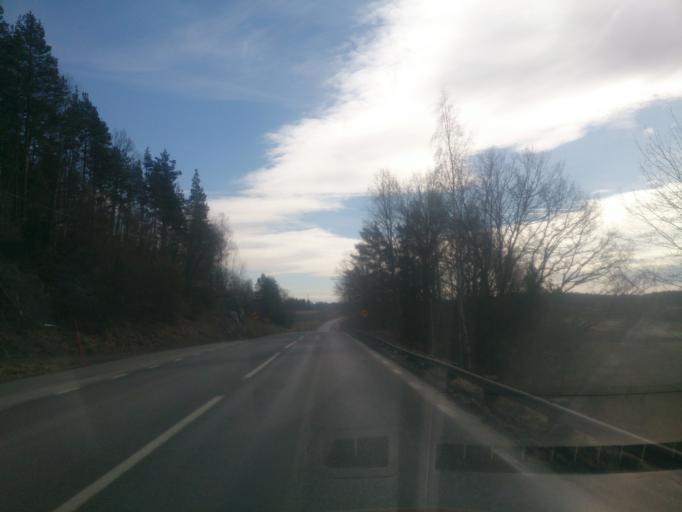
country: SE
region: OEstergoetland
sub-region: Norrkopings Kommun
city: Skarblacka
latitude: 58.6071
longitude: 15.8185
